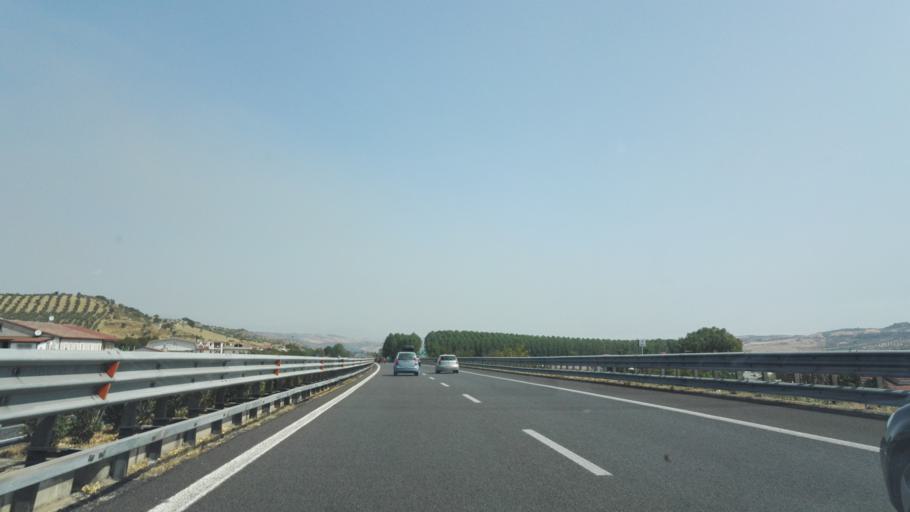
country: IT
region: Calabria
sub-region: Provincia di Cosenza
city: Sartano
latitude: 39.5349
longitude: 16.2224
